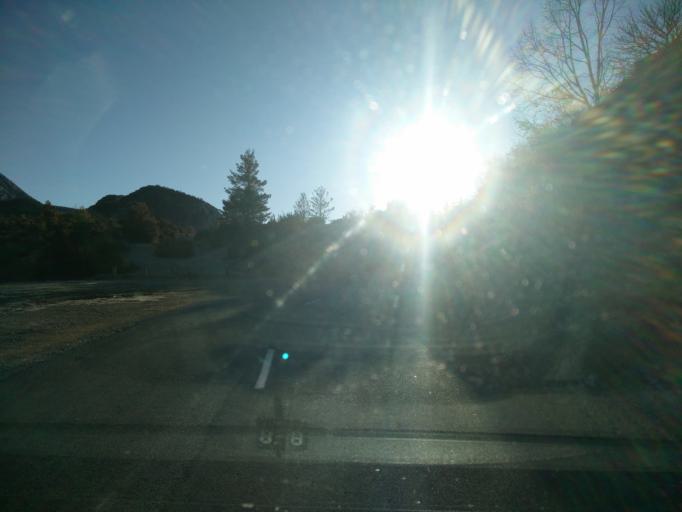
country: FR
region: Provence-Alpes-Cote d'Azur
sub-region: Departement des Alpes-de-Haute-Provence
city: Castellane
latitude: 43.7943
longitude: 6.3994
